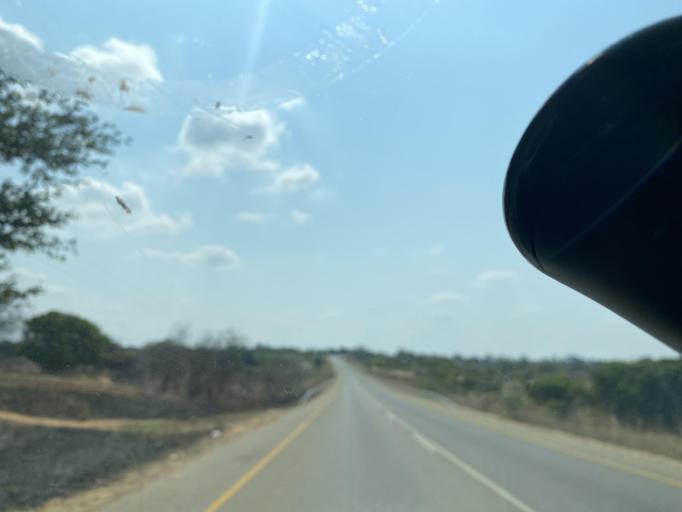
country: ZM
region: Lusaka
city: Chongwe
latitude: -15.5283
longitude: 28.6112
